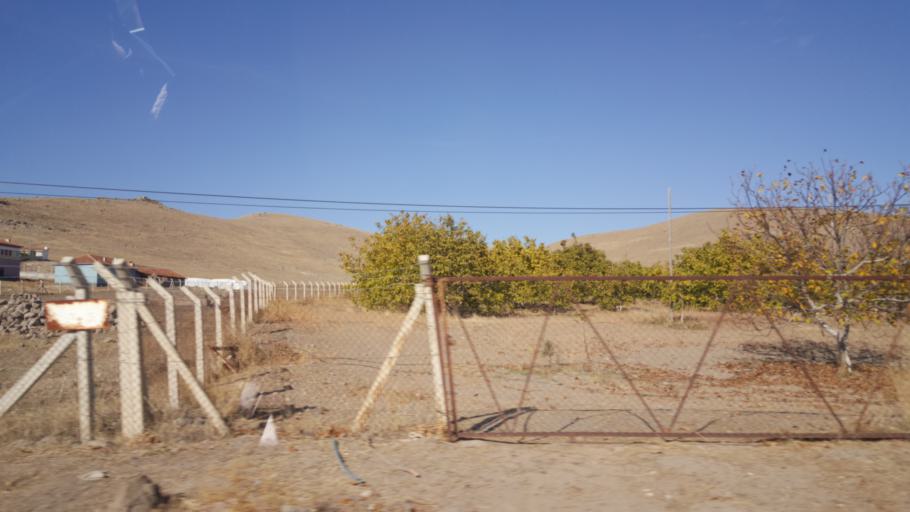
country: TR
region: Ankara
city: Altpinar
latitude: 39.1708
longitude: 32.6933
